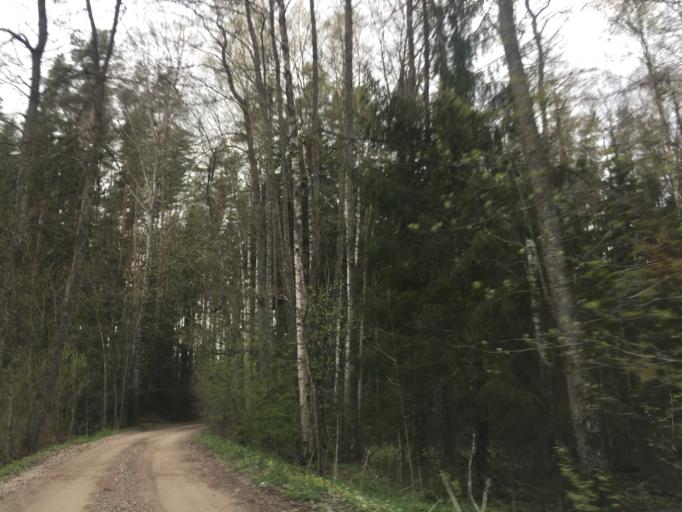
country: LV
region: Lecava
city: Iecava
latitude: 56.6433
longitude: 24.1788
